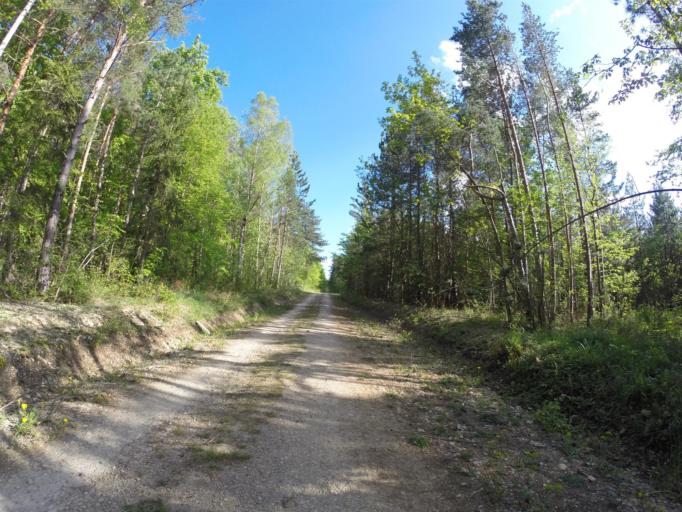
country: DE
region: Thuringia
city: Zollnitz
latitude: 50.9028
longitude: 11.6318
